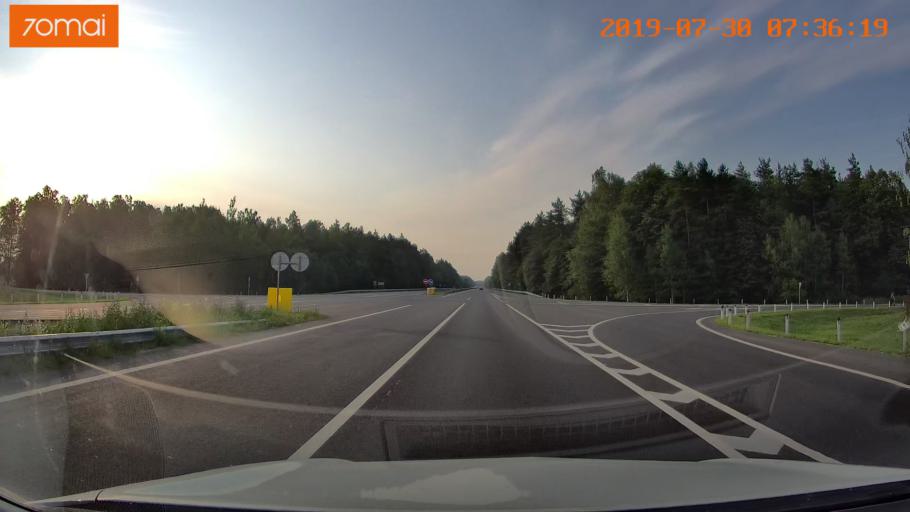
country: RU
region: Kaliningrad
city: Gvardeysk
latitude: 54.6656
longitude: 21.1216
